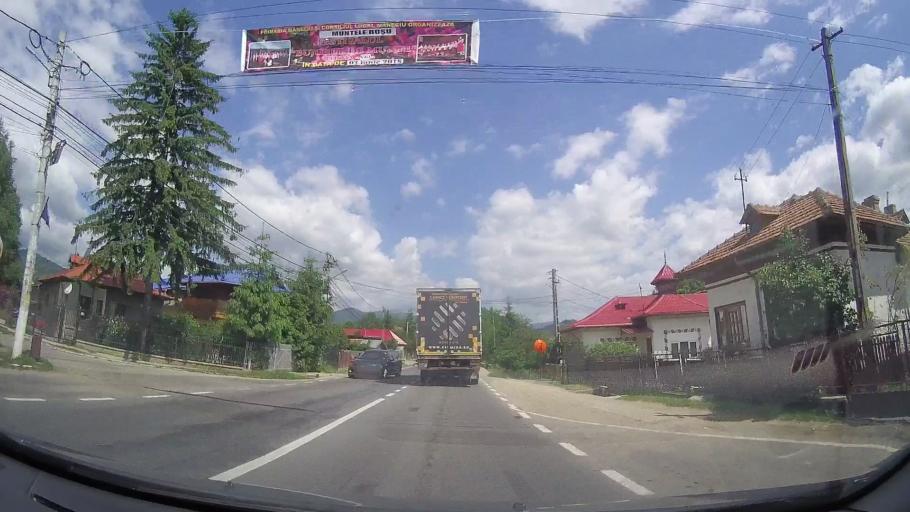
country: RO
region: Prahova
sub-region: Comuna Maneciu-Ungureni
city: Gheaba
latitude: 45.2917
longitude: 25.9993
